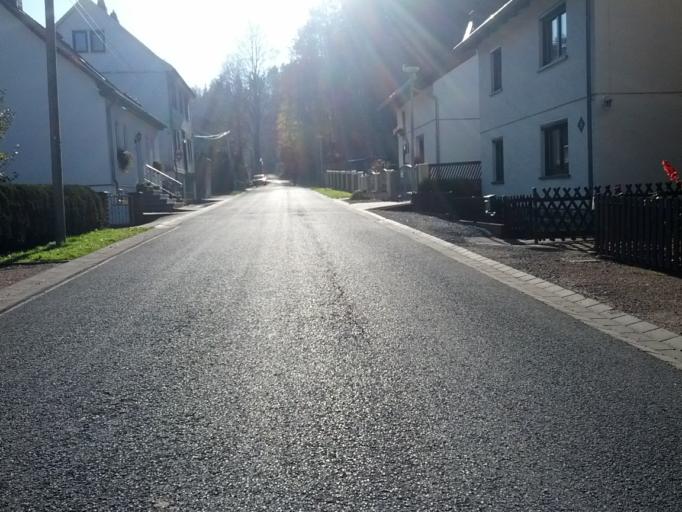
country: DE
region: Thuringia
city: Thal
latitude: 50.9116
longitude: 10.4003
